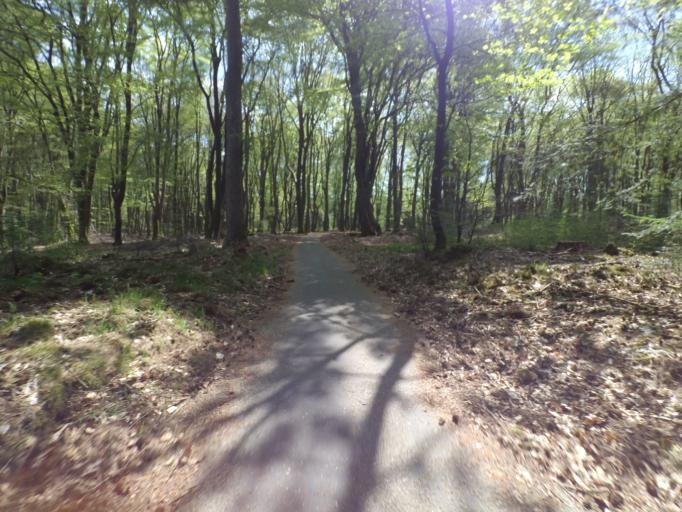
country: NL
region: Gelderland
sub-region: Gemeente Barneveld
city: Garderen
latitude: 52.2531
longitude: 5.6948
